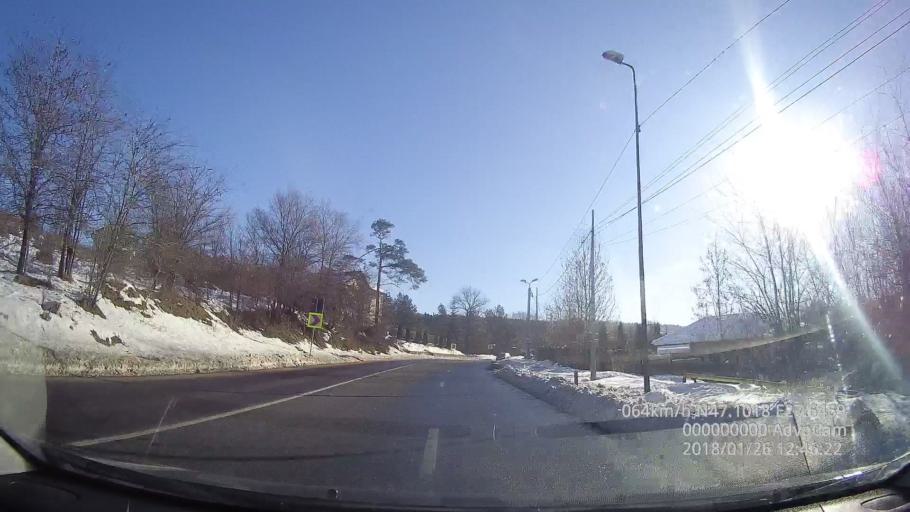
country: RO
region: Iasi
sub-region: Comuna Tomesti
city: Tomesti
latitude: 47.1015
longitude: 27.6475
